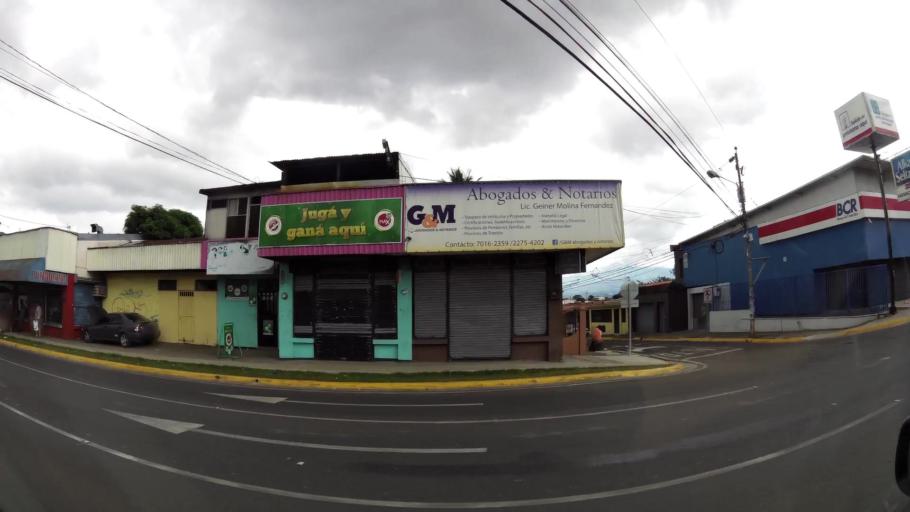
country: CR
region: San Jose
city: Alajuelita
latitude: 9.8964
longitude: -84.0854
